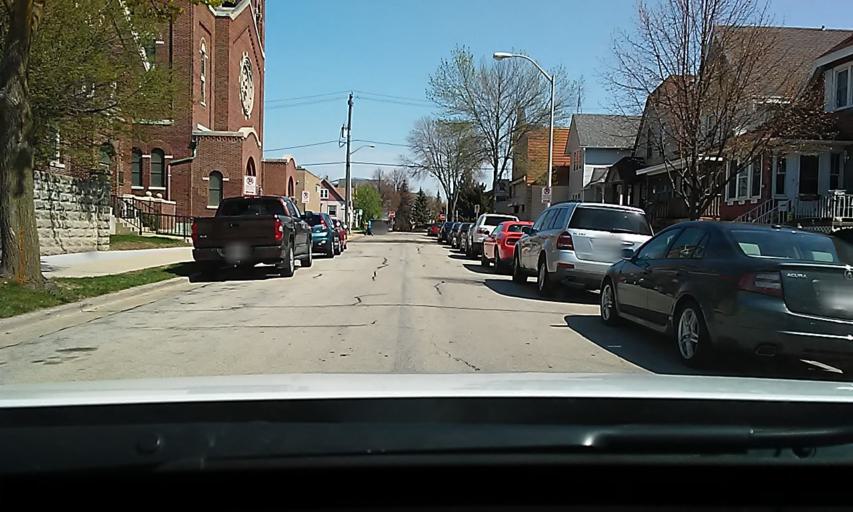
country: US
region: Wisconsin
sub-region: Milwaukee County
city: West Milwaukee
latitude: 43.0179
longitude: -87.9699
